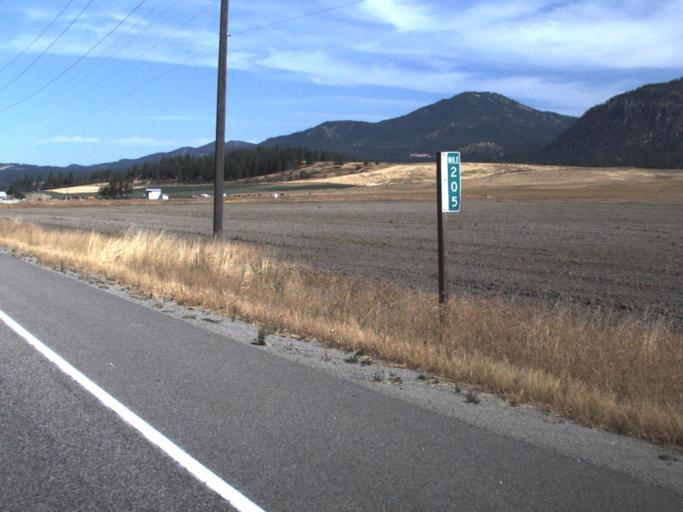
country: US
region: Washington
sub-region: Stevens County
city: Chewelah
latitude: 48.2452
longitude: -117.7152
